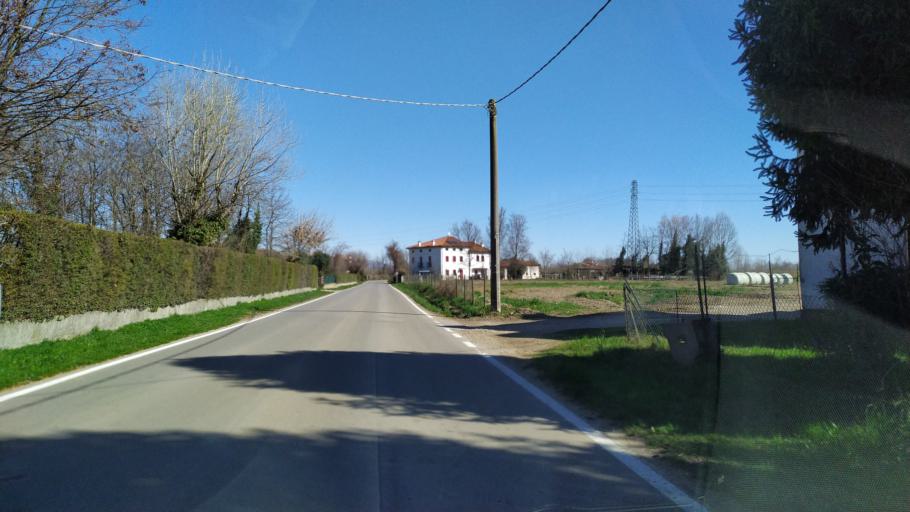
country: IT
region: Veneto
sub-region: Provincia di Vicenza
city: Sandrigo
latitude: 45.6347
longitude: 11.5934
